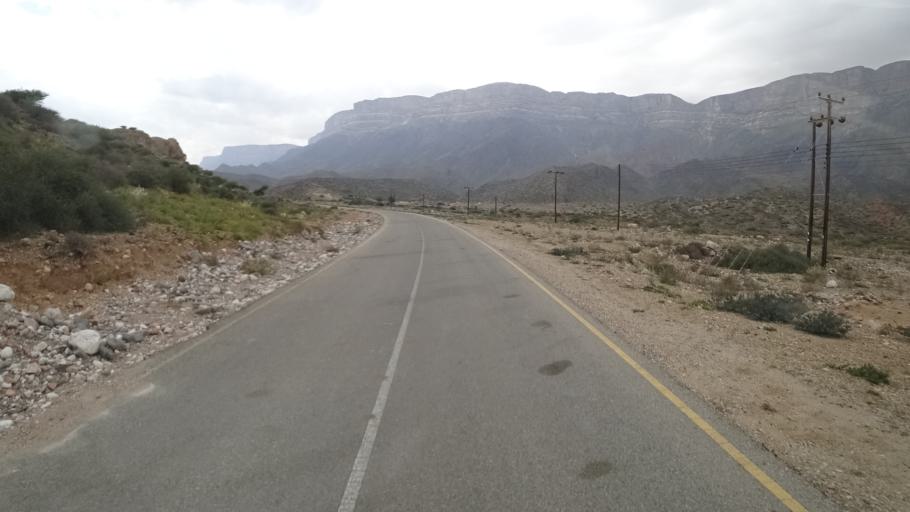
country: OM
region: Zufar
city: Salalah
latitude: 17.1738
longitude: 54.9673
